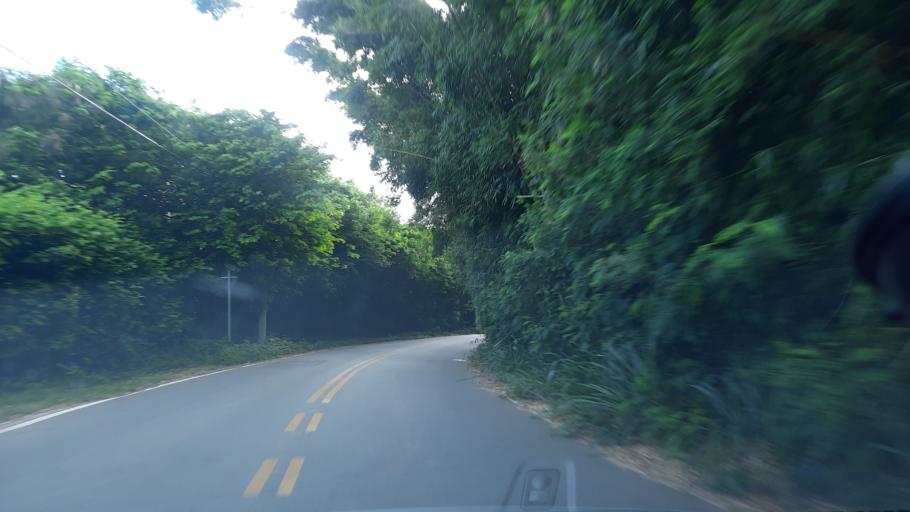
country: BR
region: Sao Paulo
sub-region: Atibaia
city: Atibaia
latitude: -23.0996
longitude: -46.5197
